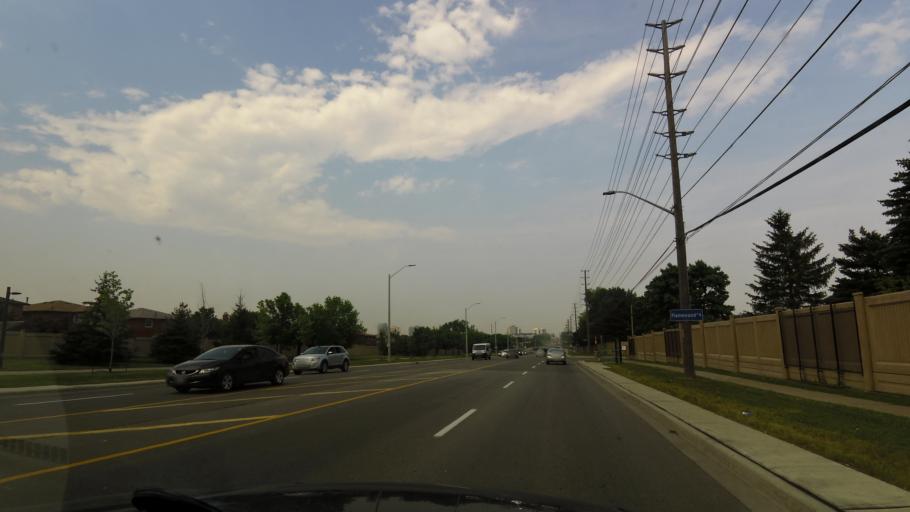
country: CA
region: Ontario
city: Mississauga
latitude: 43.6117
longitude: -79.6143
